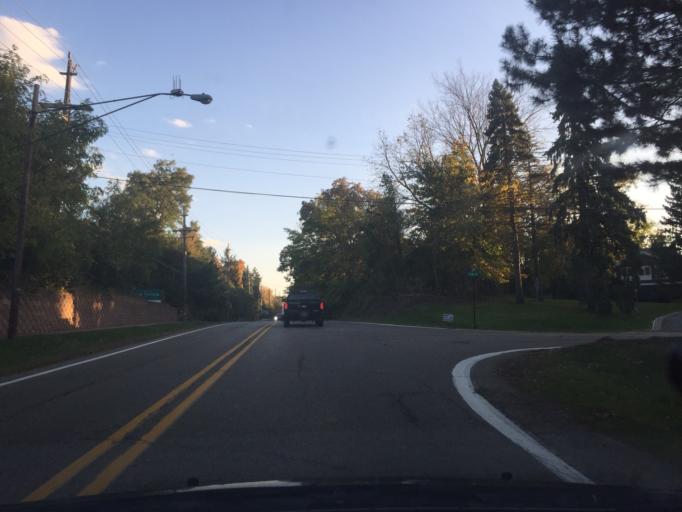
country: US
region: Michigan
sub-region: Oakland County
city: Bloomfield Hills
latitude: 42.5920
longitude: -83.2870
